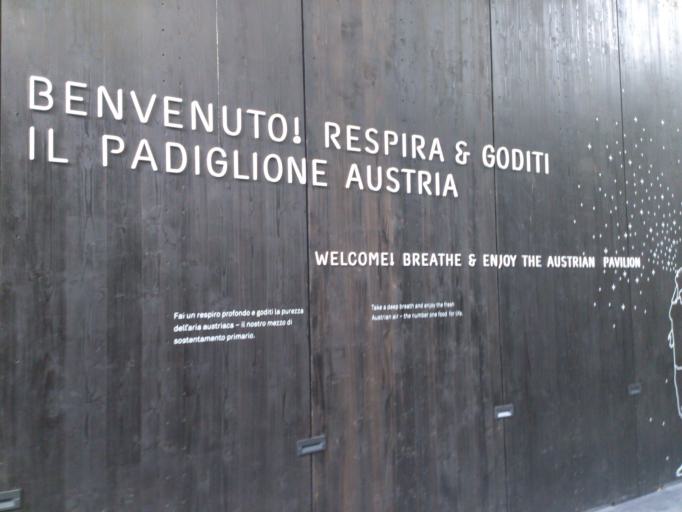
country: IT
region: Lombardy
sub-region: Citta metropolitana di Milano
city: Baranzate
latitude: 45.5174
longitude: 9.1068
